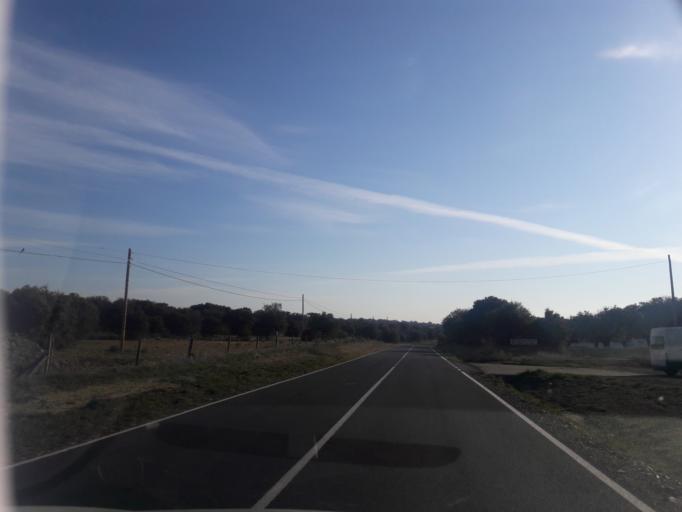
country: ES
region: Castille and Leon
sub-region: Provincia de Salamanca
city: Guijuelo
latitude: 40.5760
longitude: -5.6495
